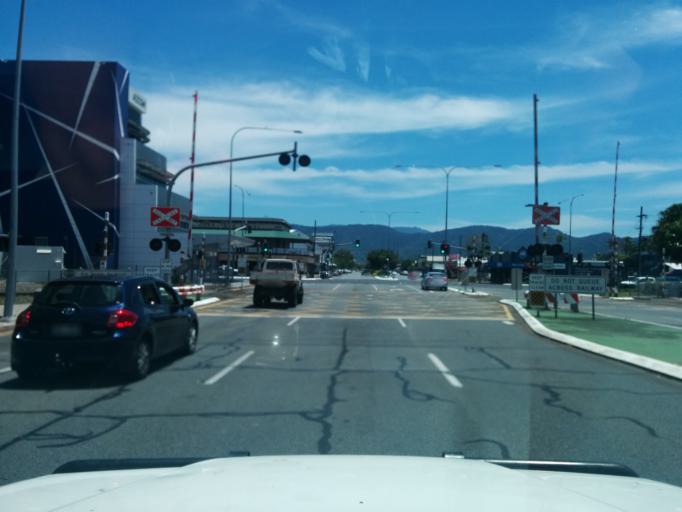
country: AU
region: Queensland
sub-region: Cairns
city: Cairns
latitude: -16.9272
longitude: 145.7730
